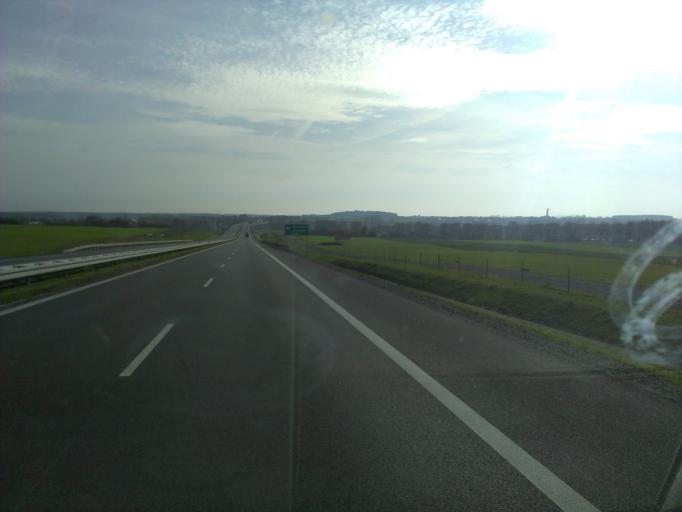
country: PL
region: Lubusz
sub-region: Powiat swiebodzinski
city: Swiebodzin
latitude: 52.2628
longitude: 15.5452
